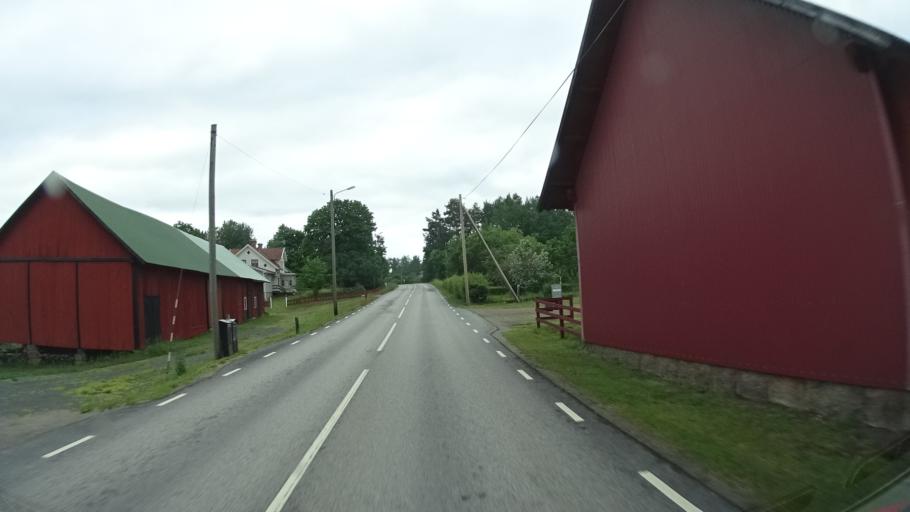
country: SE
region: Kalmar
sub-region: Oskarshamns Kommun
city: Oskarshamn
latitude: 57.3536
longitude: 16.2405
